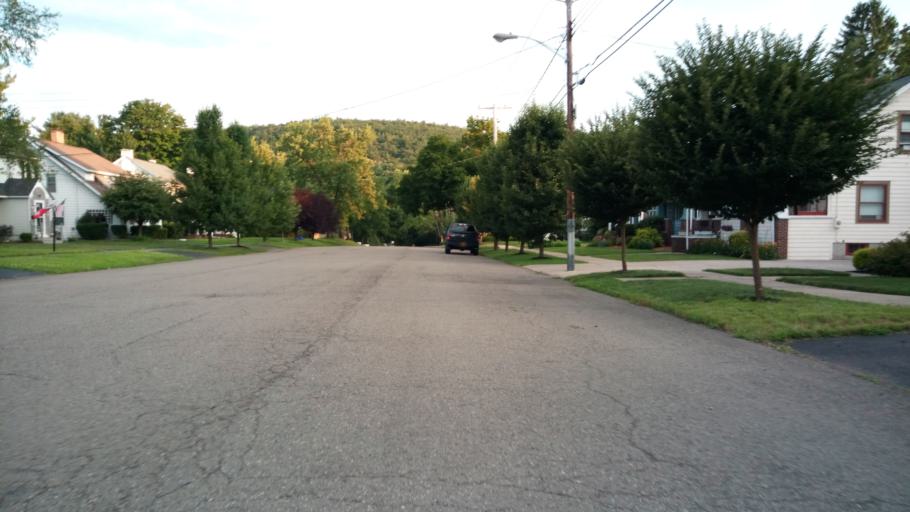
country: US
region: New York
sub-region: Chemung County
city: West Elmira
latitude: 42.0771
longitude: -76.8485
